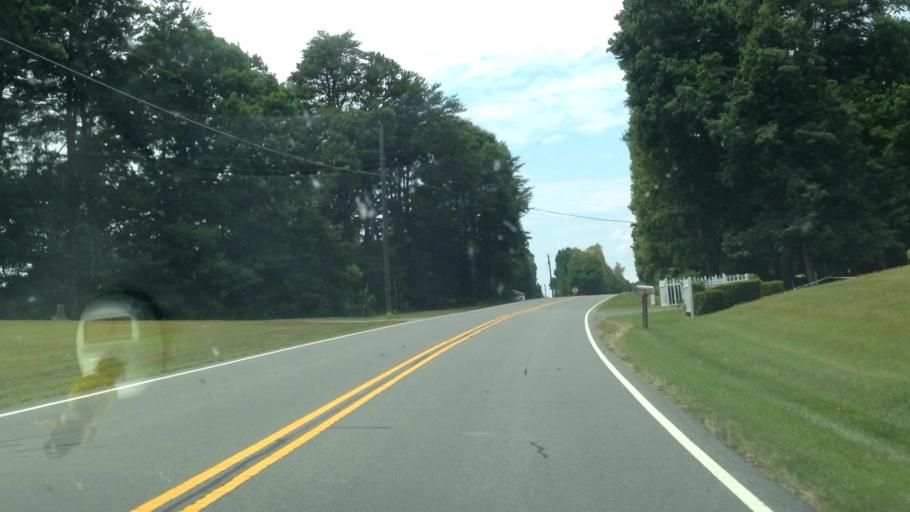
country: US
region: North Carolina
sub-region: Stokes County
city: Walnut Cove
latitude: 36.3718
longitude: -80.0814
